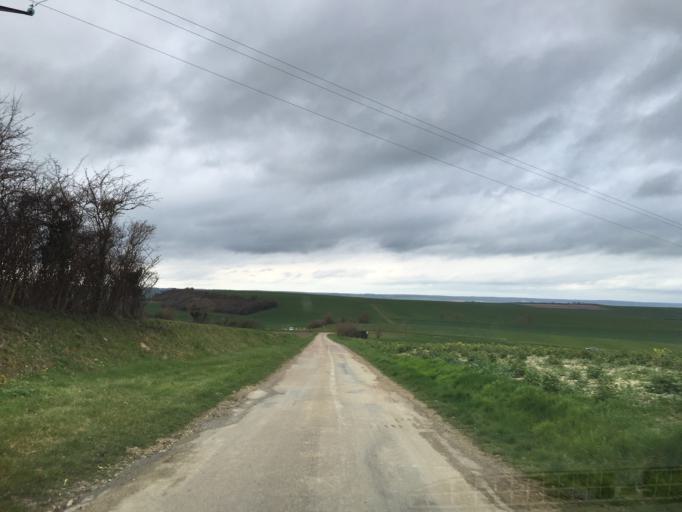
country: FR
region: Bourgogne
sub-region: Departement de l'Yonne
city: Pourrain
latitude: 47.7947
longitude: 3.4155
